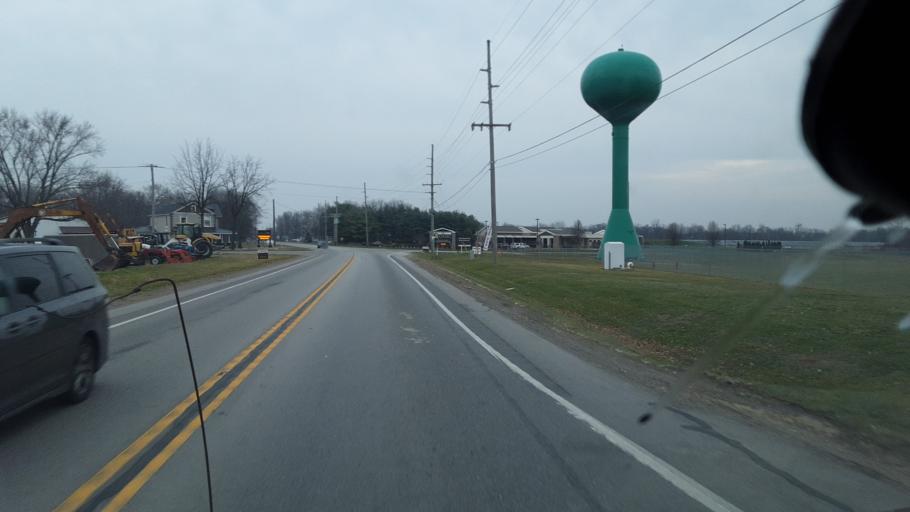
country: US
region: Indiana
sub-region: Elkhart County
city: Middlebury
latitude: 41.6955
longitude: -85.6927
